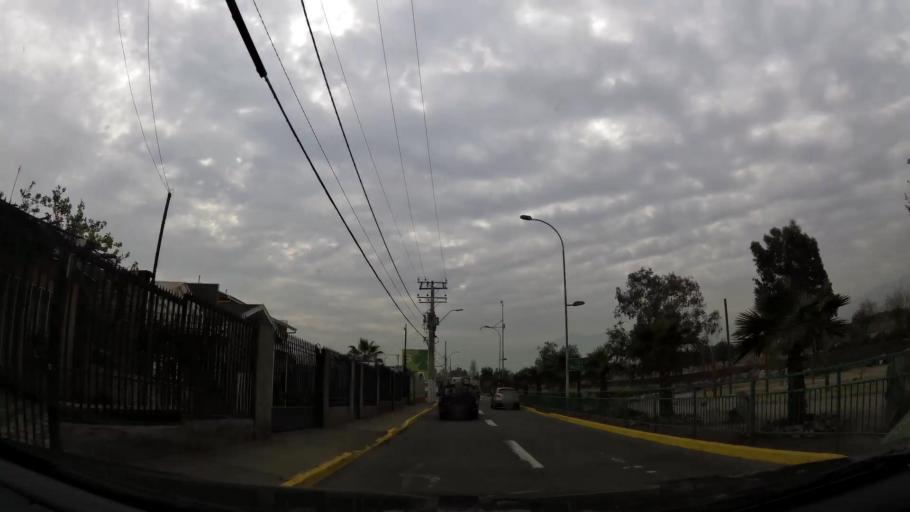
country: CL
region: Santiago Metropolitan
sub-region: Provincia de Chacabuco
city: Chicureo Abajo
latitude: -33.2059
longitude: -70.6690
